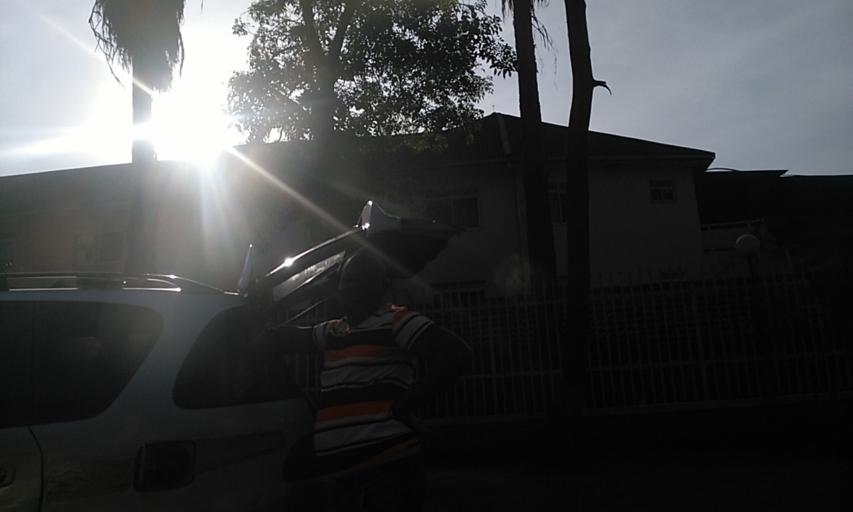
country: UG
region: Central Region
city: Kampala Central Division
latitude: 0.3242
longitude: 32.5733
